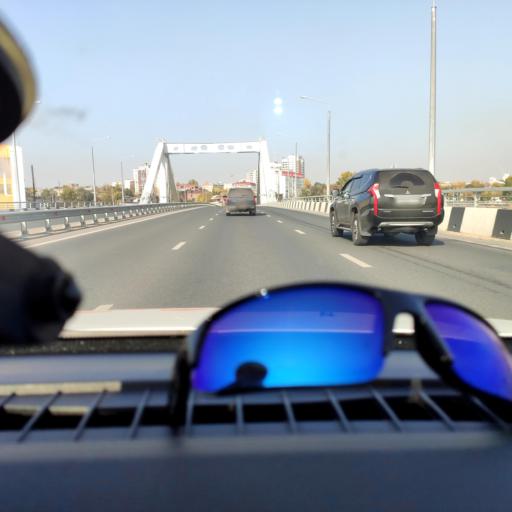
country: RU
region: Samara
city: Rozhdestveno
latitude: 53.1757
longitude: 50.0859
